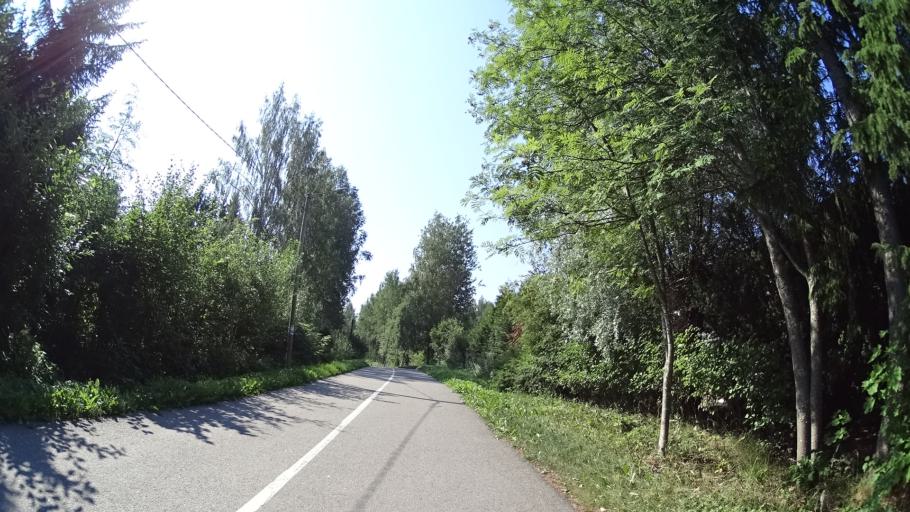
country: FI
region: Uusimaa
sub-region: Helsinki
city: Kerava
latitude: 60.3890
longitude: 25.0936
